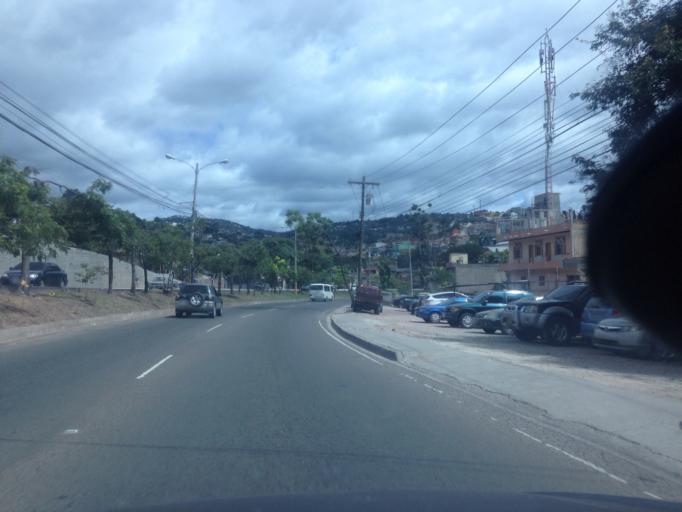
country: HN
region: Francisco Morazan
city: El Tablon
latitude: 14.0728
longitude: -87.1659
